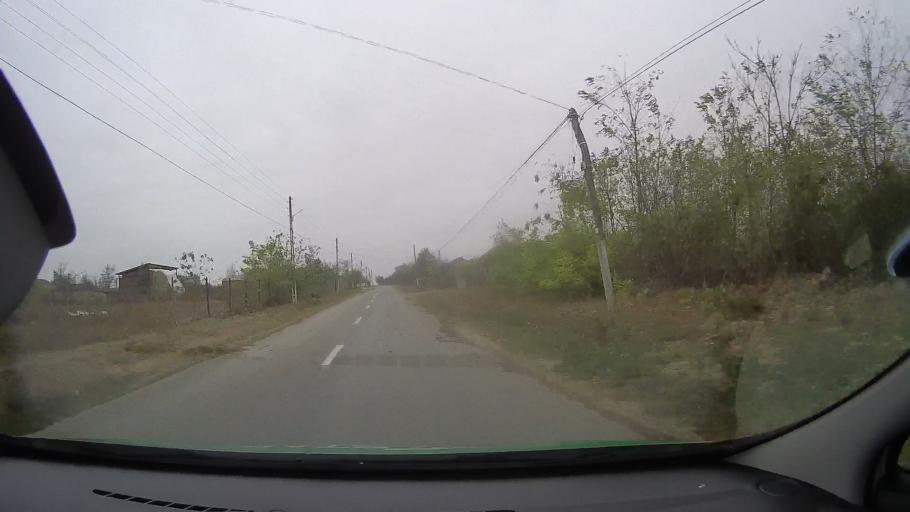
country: RO
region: Constanta
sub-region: Comuna Vulturu
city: Vulturu
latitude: 44.6512
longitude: 28.2682
